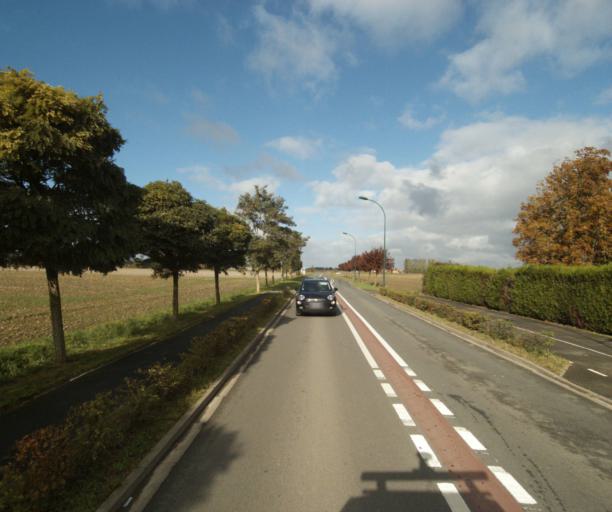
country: FR
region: Nord-Pas-de-Calais
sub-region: Departement du Nord
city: Verlinghem
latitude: 50.6877
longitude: 2.9931
